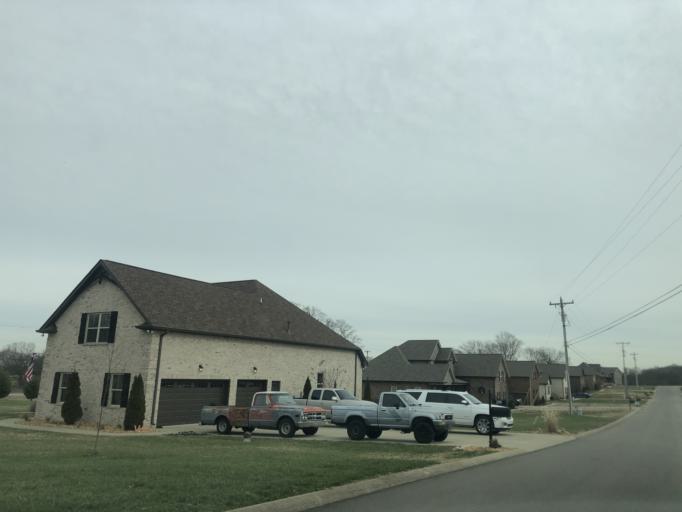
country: US
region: Tennessee
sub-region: Robertson County
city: Greenbrier
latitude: 36.4025
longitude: -86.8186
